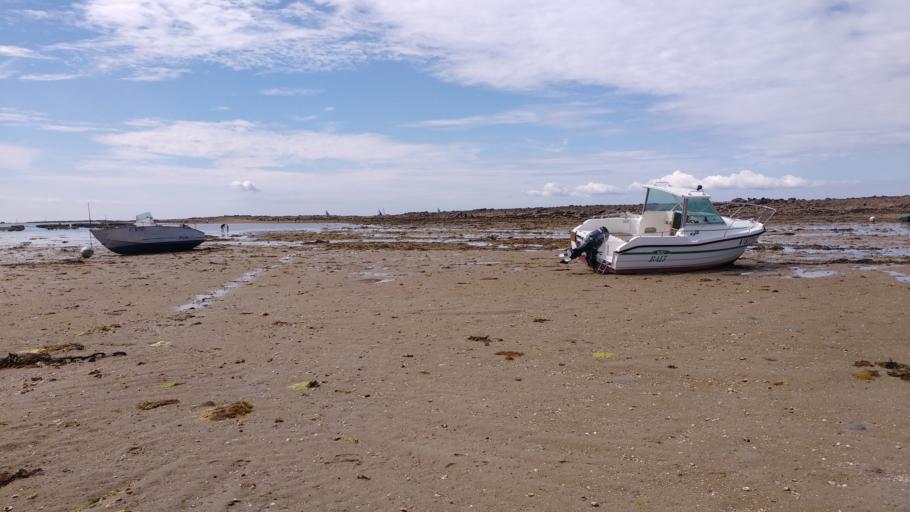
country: FR
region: Brittany
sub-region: Departement du Morbihan
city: Saint-Philibert
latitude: 47.5680
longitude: -2.9942
